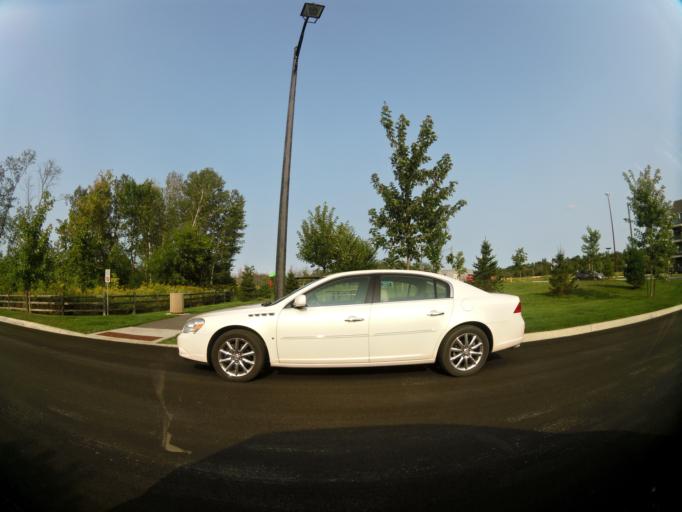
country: CA
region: Quebec
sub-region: Outaouais
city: Gatineau
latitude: 45.4906
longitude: -75.4957
